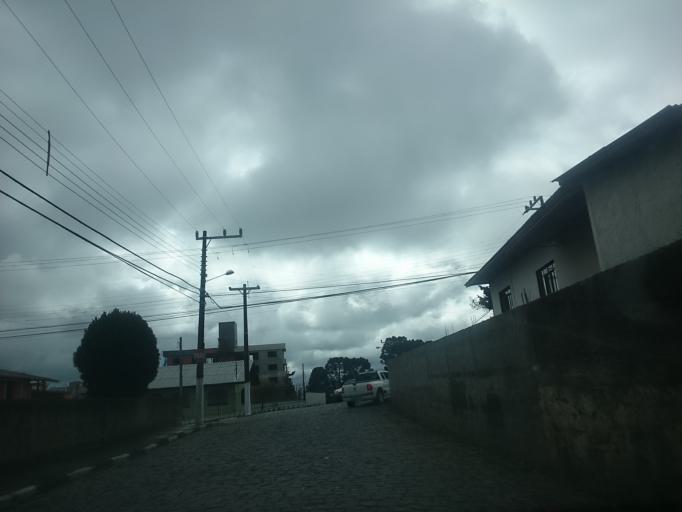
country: BR
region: Santa Catarina
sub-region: Lages
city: Lages
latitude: -27.8261
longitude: -50.3290
